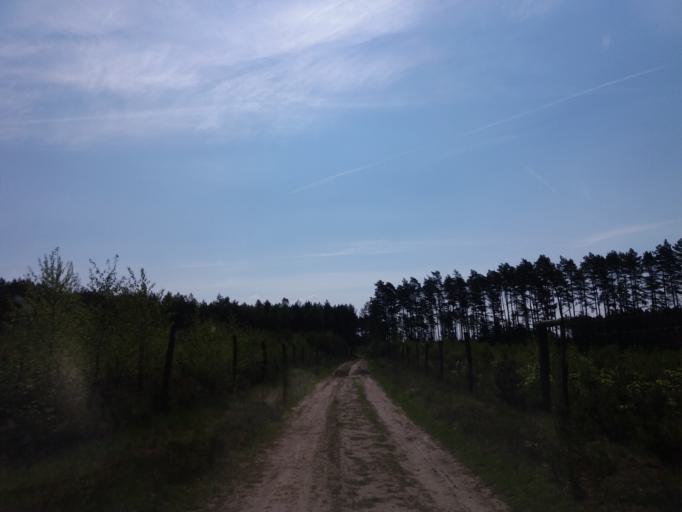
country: PL
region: West Pomeranian Voivodeship
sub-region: Powiat choszczenski
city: Bierzwnik
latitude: 53.1057
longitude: 15.7028
